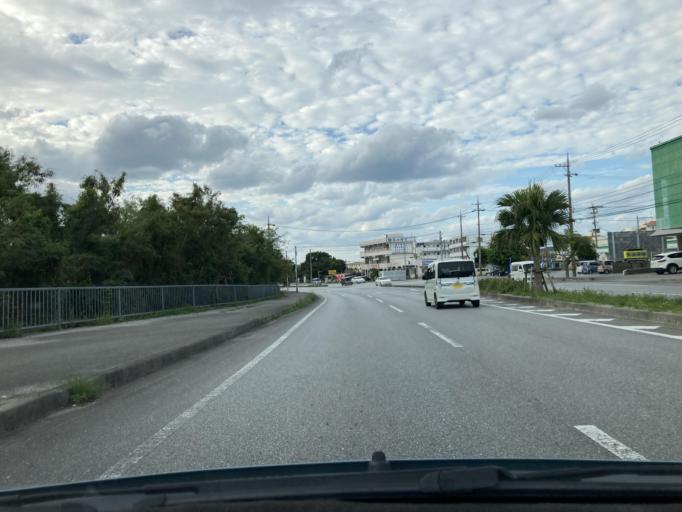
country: JP
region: Okinawa
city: Okinawa
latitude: 26.3591
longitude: 127.8002
